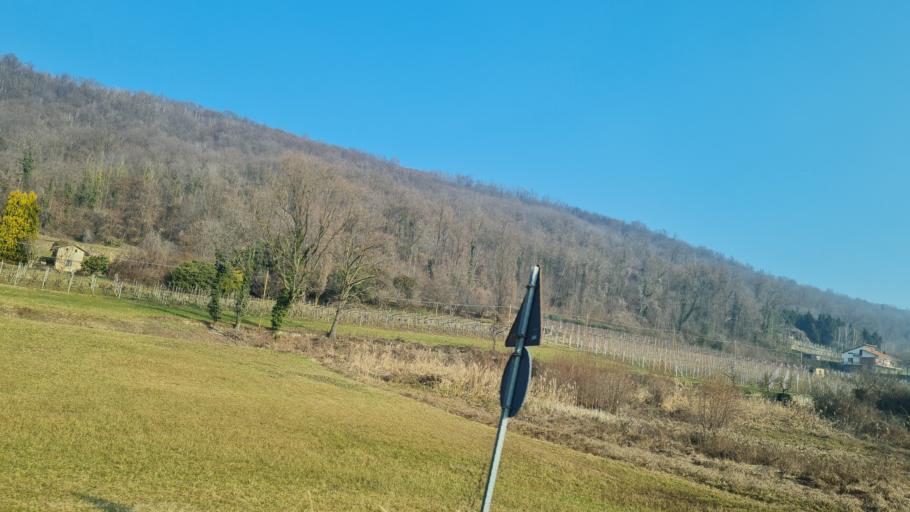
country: IT
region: Piedmont
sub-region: Provincia di Torino
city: Piverone
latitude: 45.4474
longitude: 8.0161
